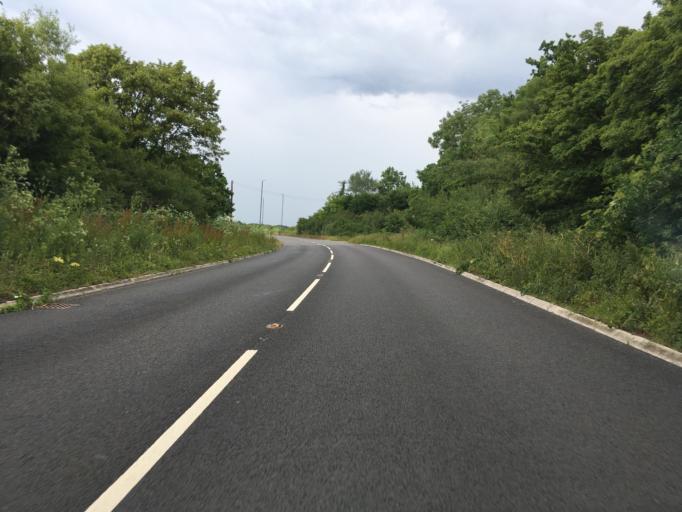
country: GB
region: England
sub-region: Gloucestershire
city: Stonehouse
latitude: 51.7913
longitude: -2.2882
